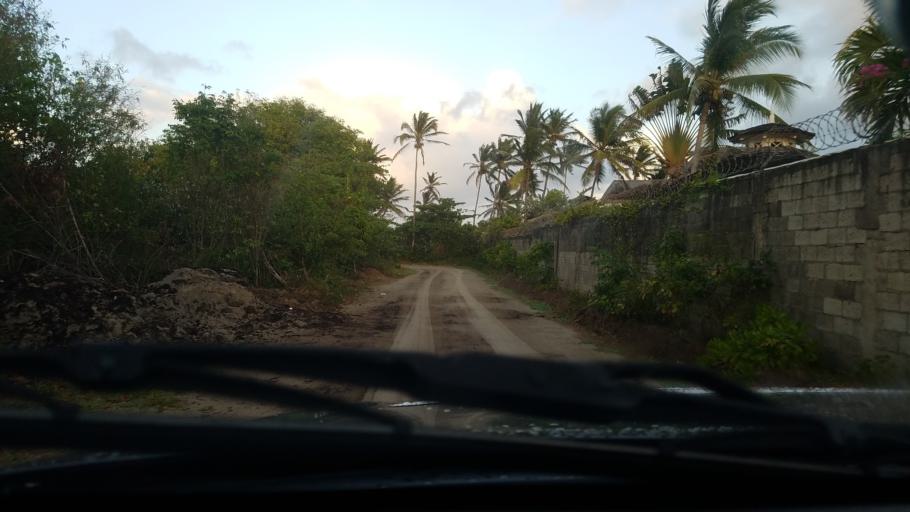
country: LC
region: Gros-Islet
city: Gros Islet
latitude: 14.0908
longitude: -60.9289
